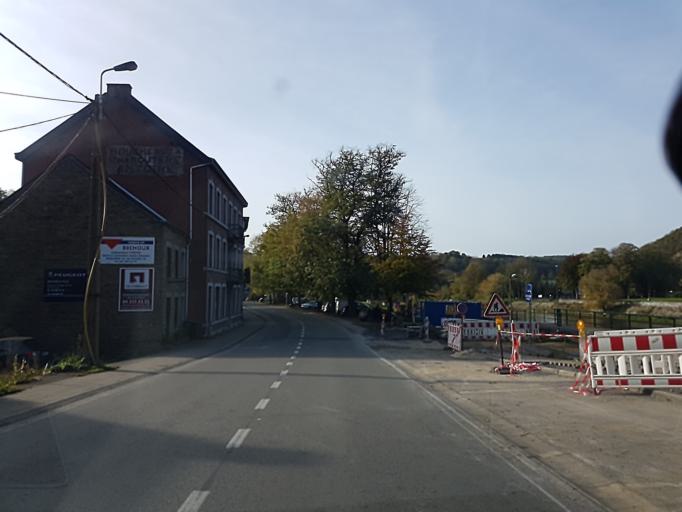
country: BE
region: Wallonia
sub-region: Province de Liege
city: Esneux
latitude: 50.5317
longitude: 5.5667
